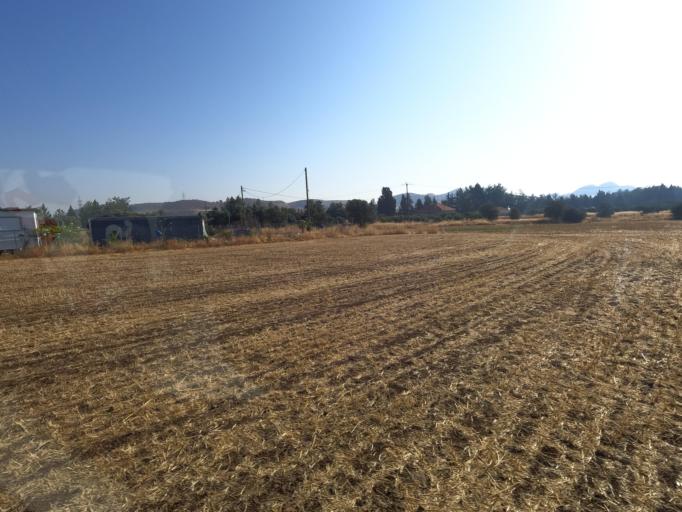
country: CY
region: Lefkosia
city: Lympia
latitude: 34.9955
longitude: 33.4348
